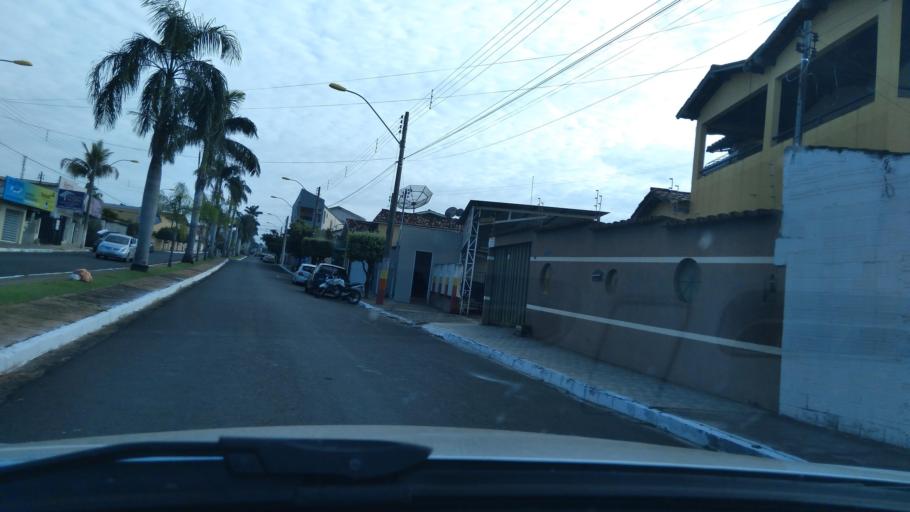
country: BR
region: Goias
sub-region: Mineiros
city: Mineiros
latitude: -17.5661
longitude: -52.5511
